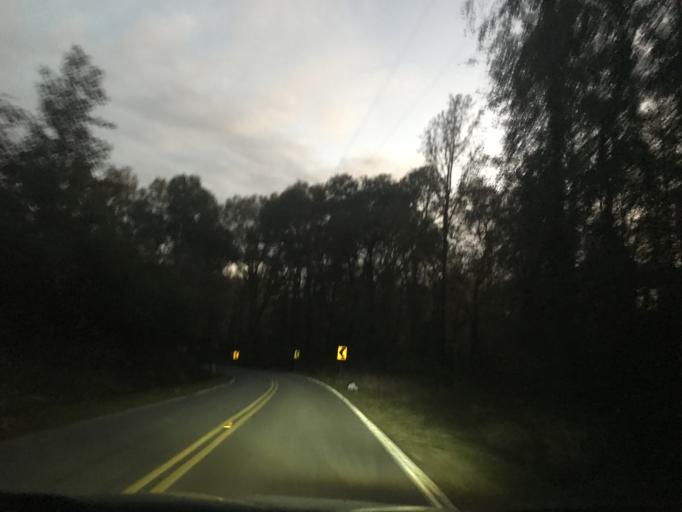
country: US
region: South Carolina
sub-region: Spartanburg County
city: Mayo
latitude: 35.0508
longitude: -81.8909
